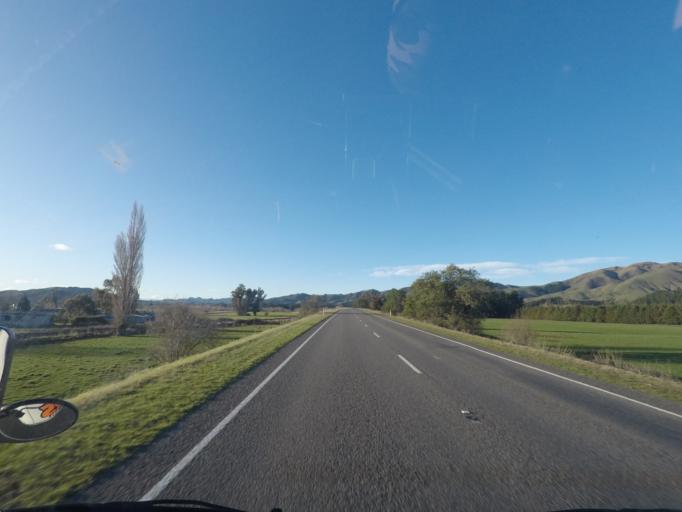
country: NZ
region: Canterbury
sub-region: Kaikoura District
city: Kaikoura
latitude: -42.7075
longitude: 173.2962
